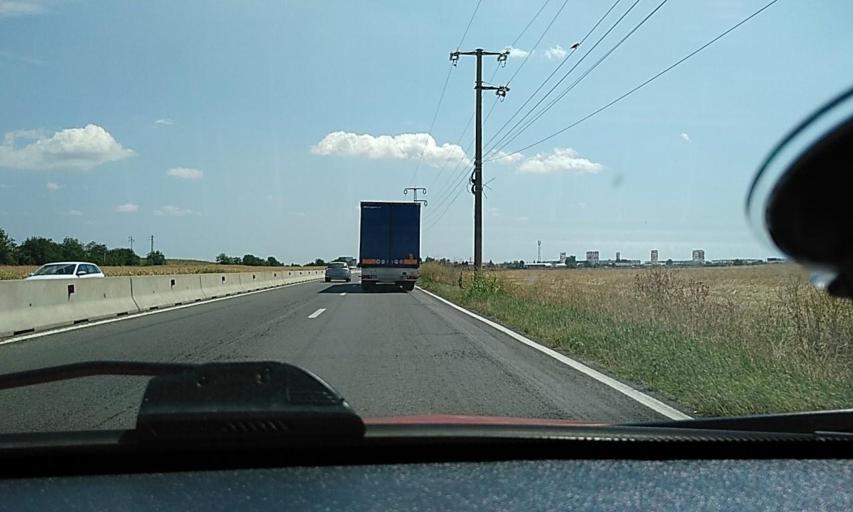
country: RO
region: Prahova
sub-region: Oras Baicoi
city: Baicoi
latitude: 45.0288
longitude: 25.8313
